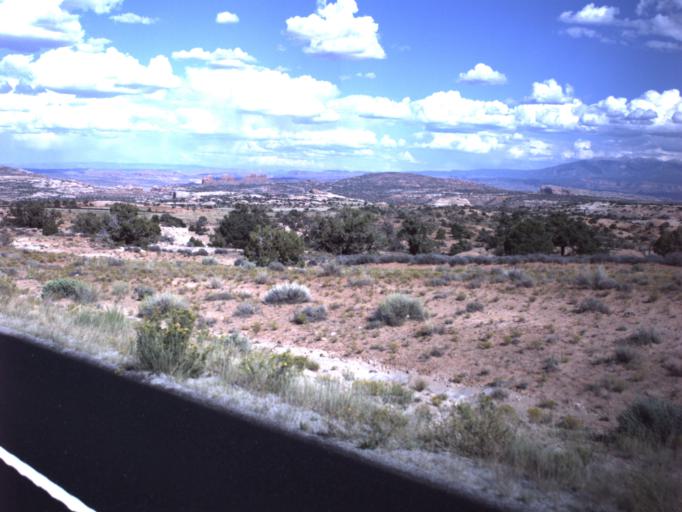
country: US
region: Utah
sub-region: Grand County
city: Moab
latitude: 38.6352
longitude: -109.7923
